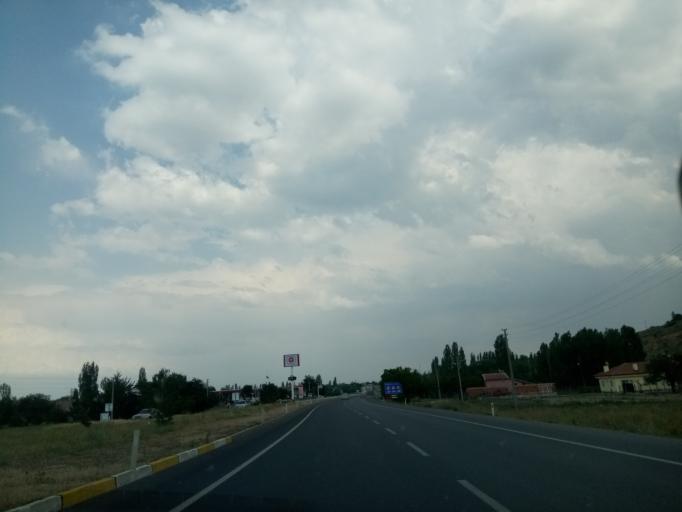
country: TR
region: Afyonkarahisar
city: Cay
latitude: 38.5908
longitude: 31.0662
